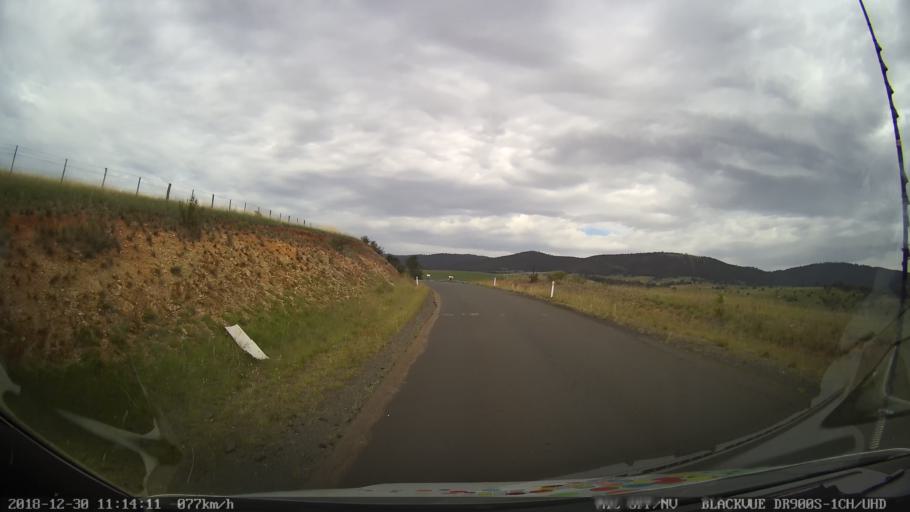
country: AU
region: New South Wales
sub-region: Snowy River
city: Jindabyne
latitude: -36.5343
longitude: 148.7324
